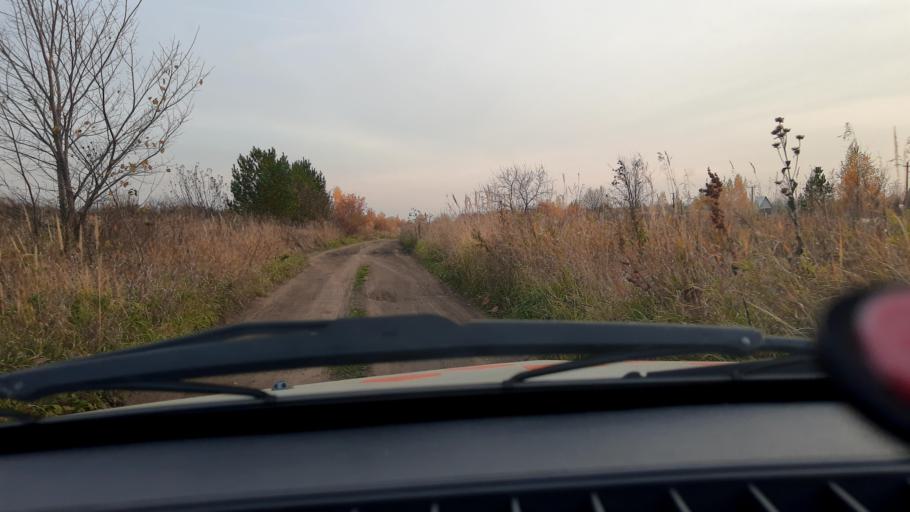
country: RU
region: Bashkortostan
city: Iglino
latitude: 54.8028
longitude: 56.3471
